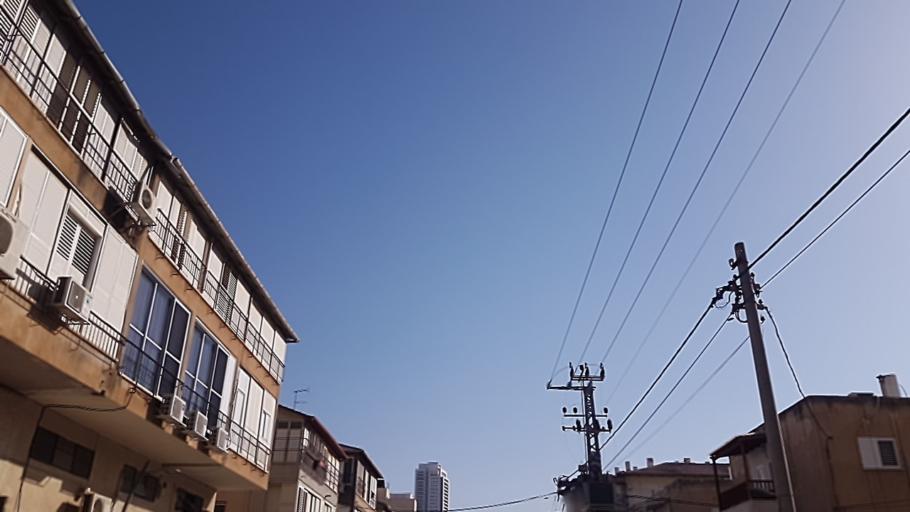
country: IL
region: Tel Aviv
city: Giv`atayim
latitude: 32.0764
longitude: 34.8231
